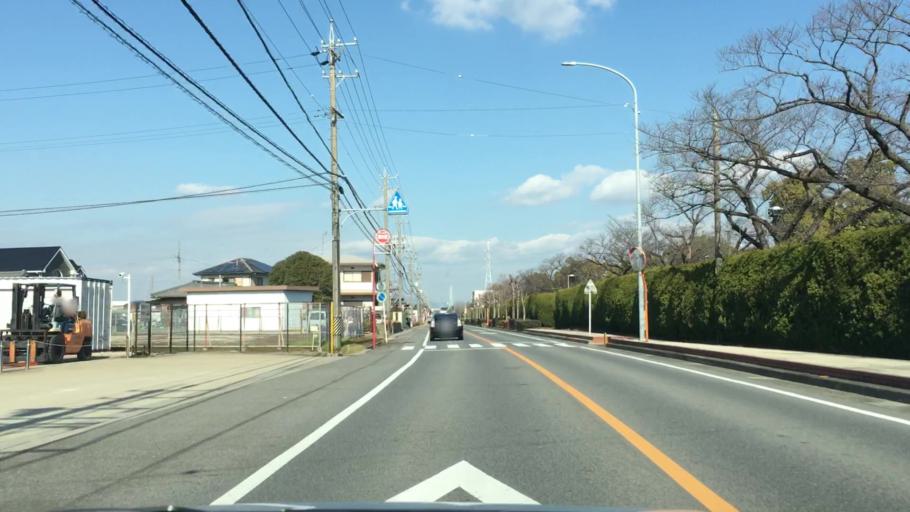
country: JP
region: Aichi
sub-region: Toyota-shi
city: Toyota
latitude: 35.0208
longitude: 137.1265
